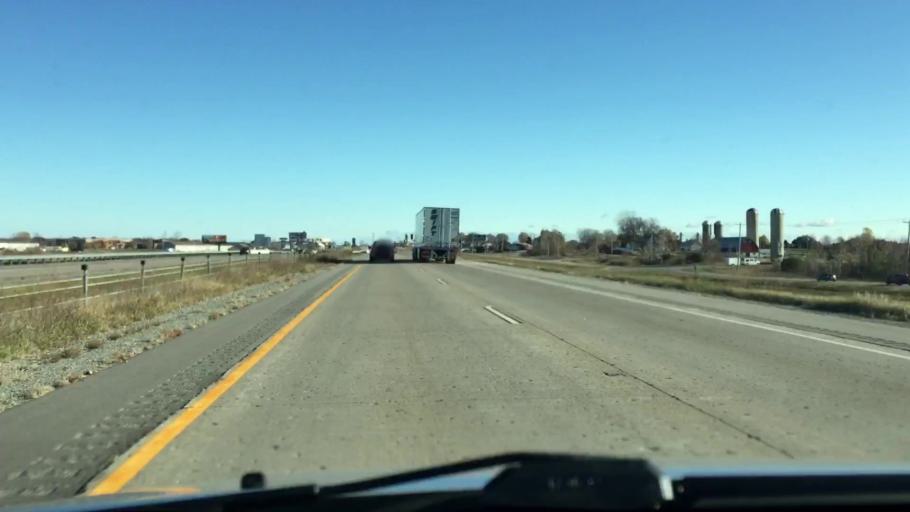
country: US
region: Wisconsin
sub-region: Outagamie County
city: Kaukauna
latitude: 44.3127
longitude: -88.2307
